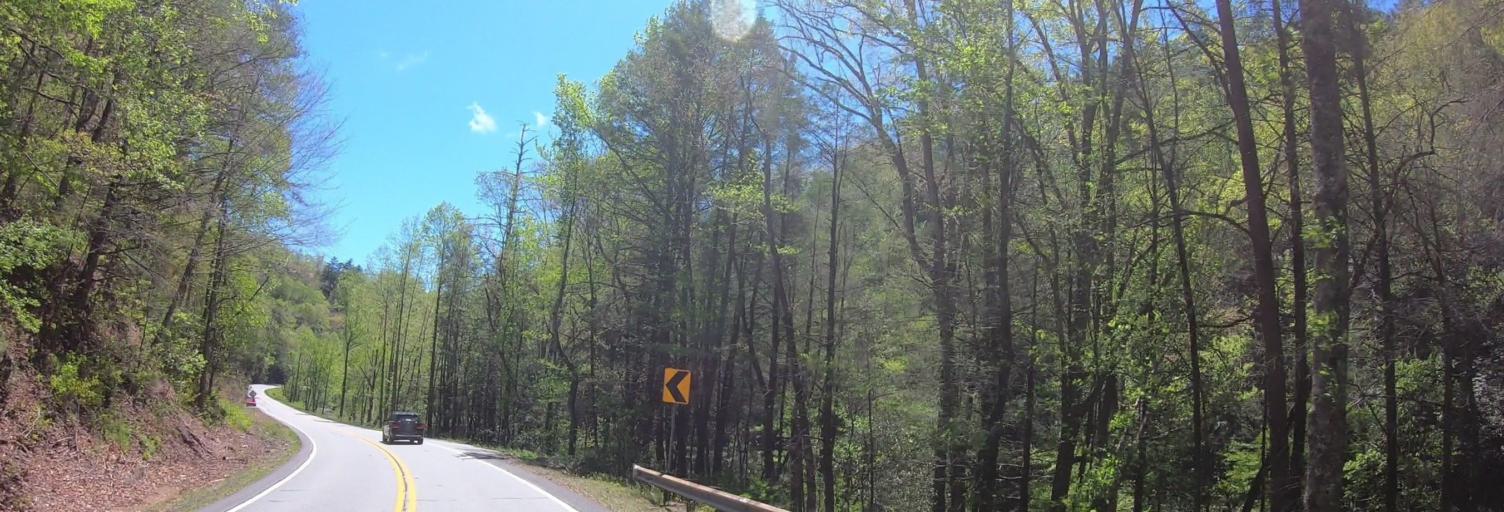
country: US
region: Georgia
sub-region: White County
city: Cleveland
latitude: 34.7249
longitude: -83.7513
